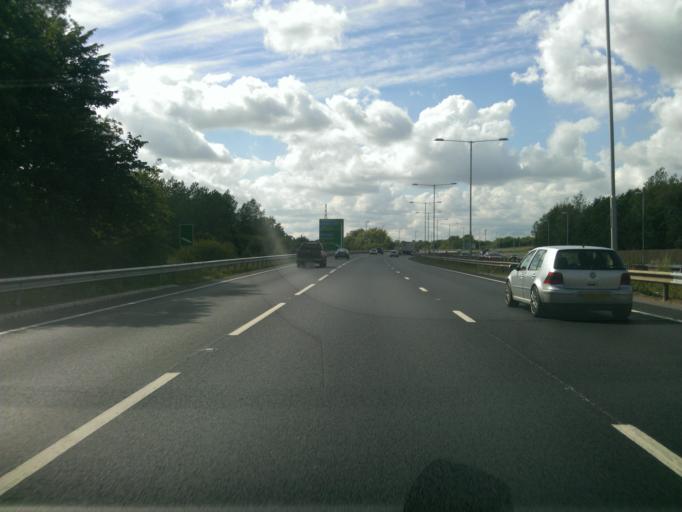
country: GB
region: England
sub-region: Northamptonshire
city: Kettering
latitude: 52.3869
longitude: -0.7399
